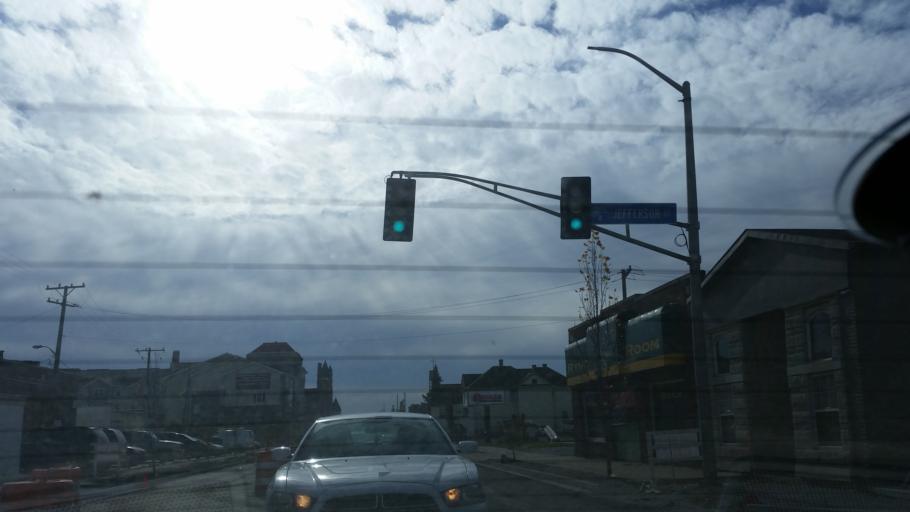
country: US
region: Indiana
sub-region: Howard County
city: Kokomo
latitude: 40.4909
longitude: -86.1337
